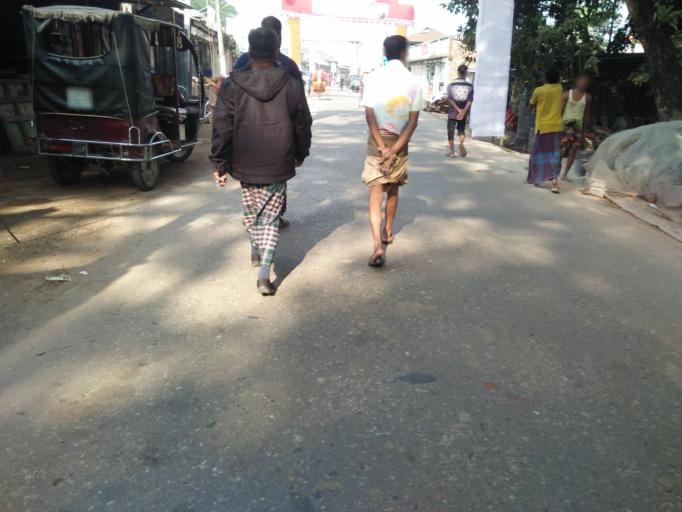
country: BD
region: Khulna
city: Uttar Char Fasson
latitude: 22.1907
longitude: 90.6757
